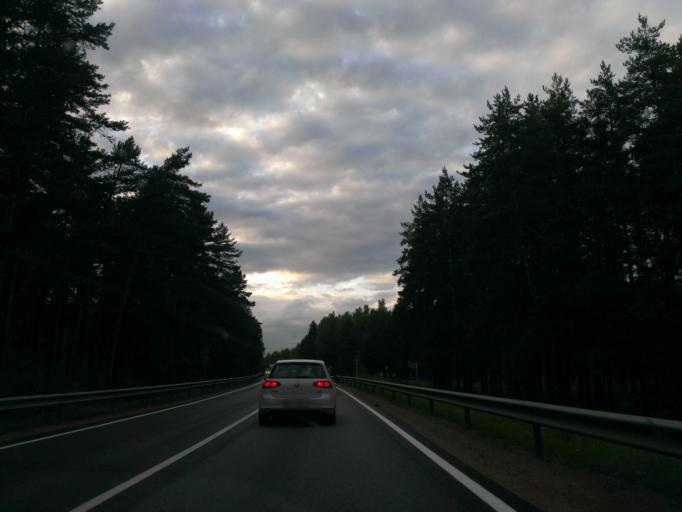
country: LV
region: Riga
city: Bergi
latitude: 56.9589
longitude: 24.3763
